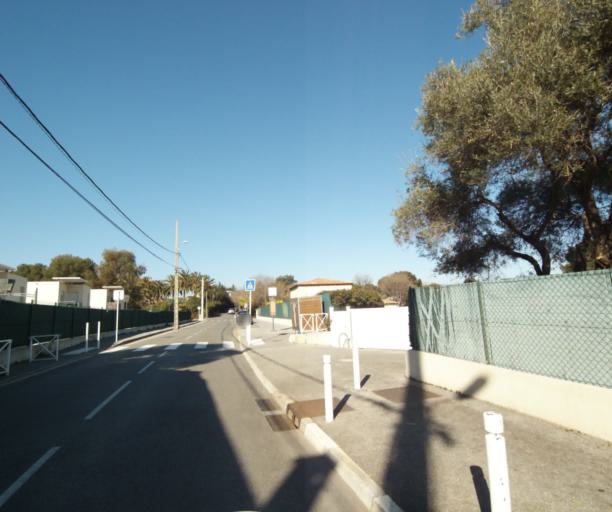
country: FR
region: Provence-Alpes-Cote d'Azur
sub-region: Departement des Alpes-Maritimes
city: Biot
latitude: 43.6004
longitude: 7.1017
